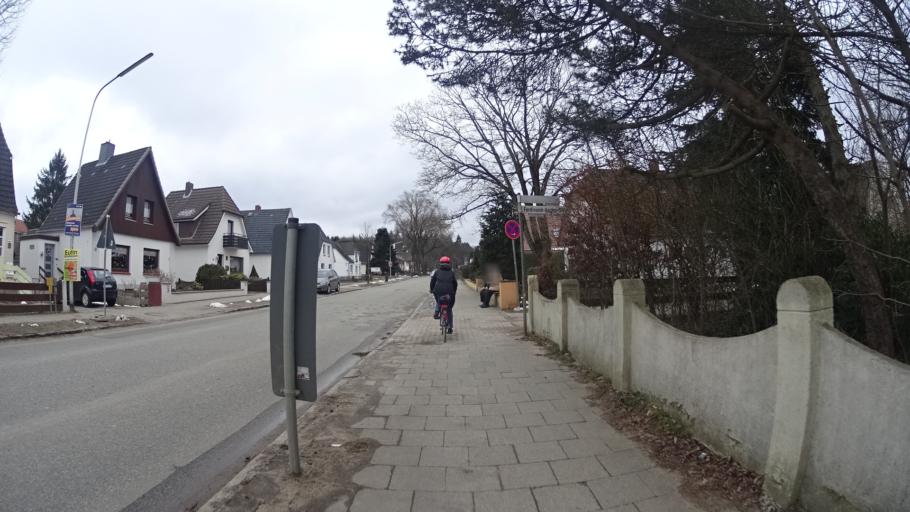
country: DE
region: Schleswig-Holstein
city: Malente
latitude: 54.1816
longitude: 10.5631
